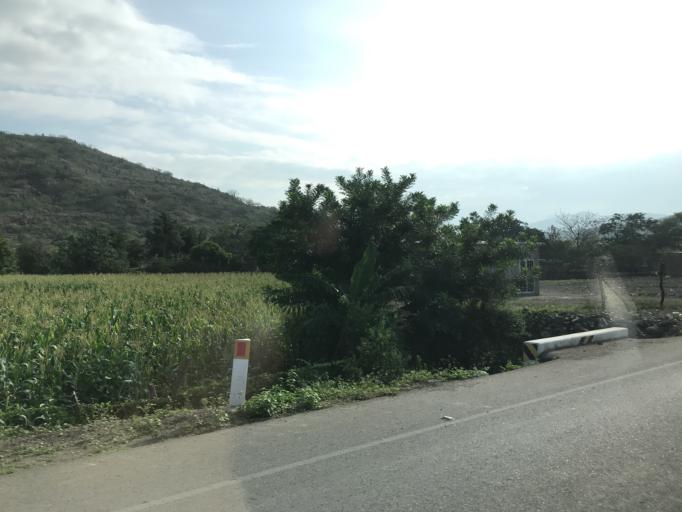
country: PE
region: Lambayeque
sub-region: Provincia de Chiclayo
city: Chongoyape
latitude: -6.6328
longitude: -79.3913
